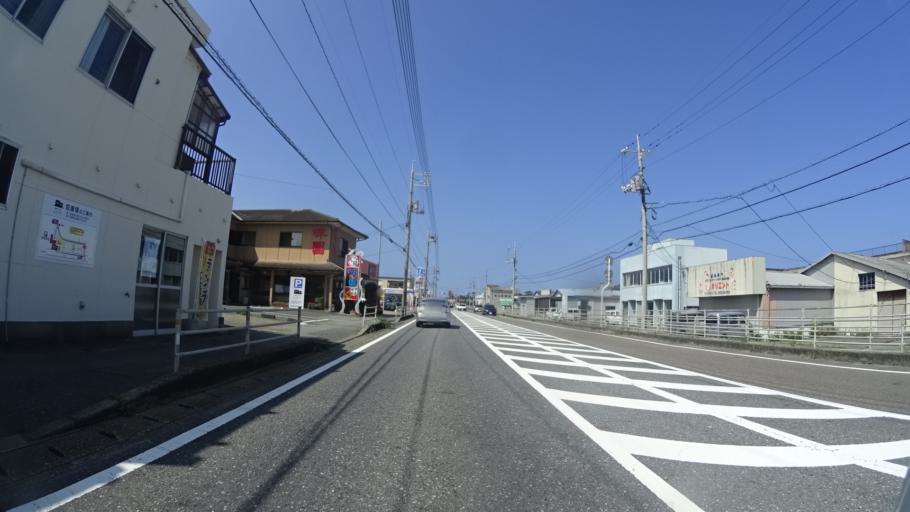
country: JP
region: Shimane
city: Masuda
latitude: 34.6900
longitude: 131.8129
